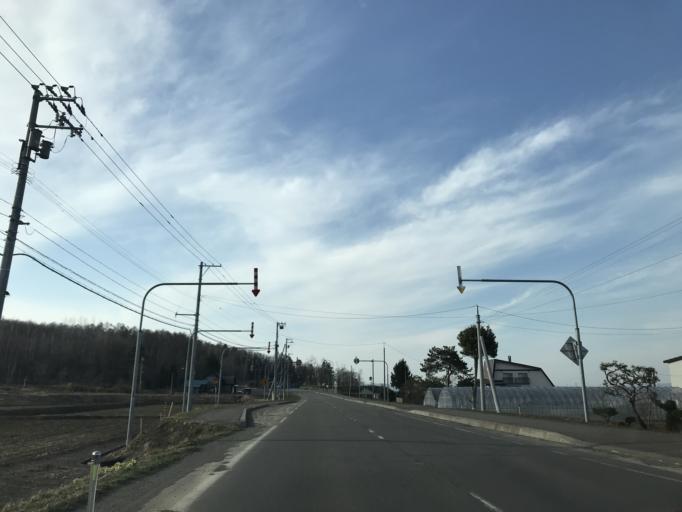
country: JP
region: Hokkaido
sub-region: Asahikawa-shi
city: Asahikawa
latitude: 43.7144
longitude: 142.3542
